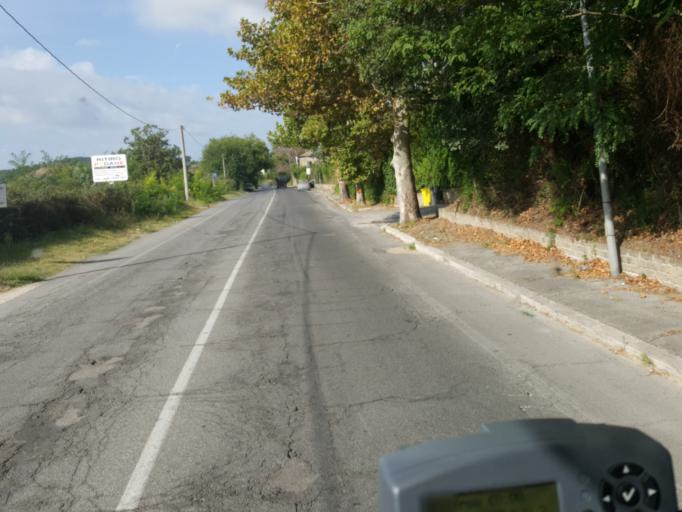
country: IT
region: Latium
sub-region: Citta metropolitana di Roma Capitale
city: Girardi-Bellavista-Terrazze
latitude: 42.0964
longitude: 12.5746
